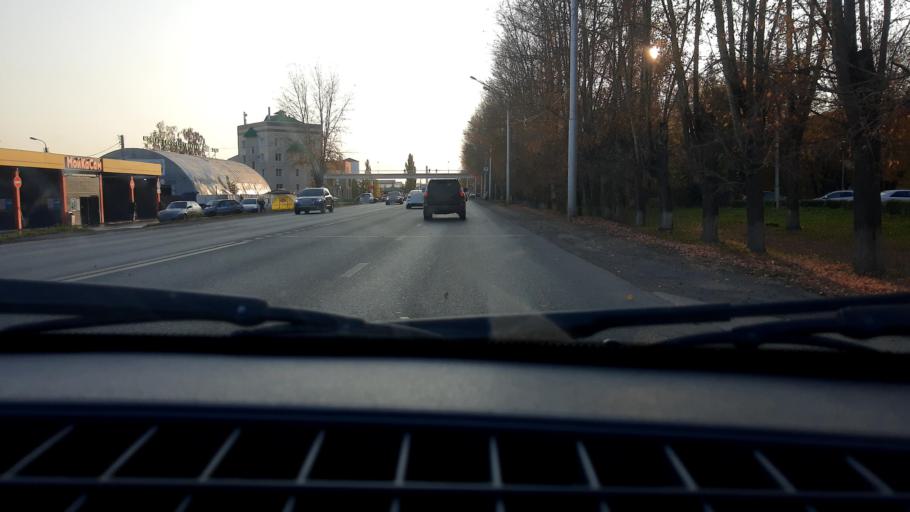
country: RU
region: Bashkortostan
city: Mikhaylovka
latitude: 54.7000
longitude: 55.8378
